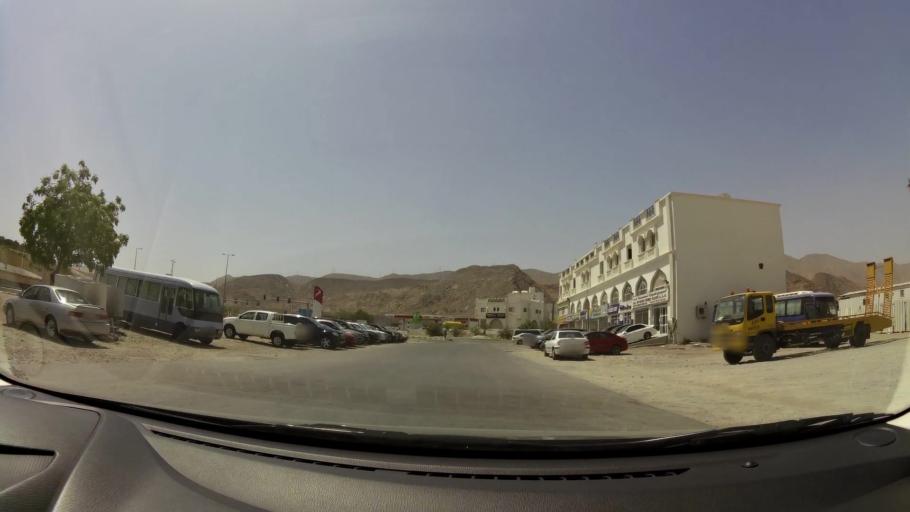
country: OM
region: Muhafazat Masqat
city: Bawshar
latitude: 23.5923
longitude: 58.4581
